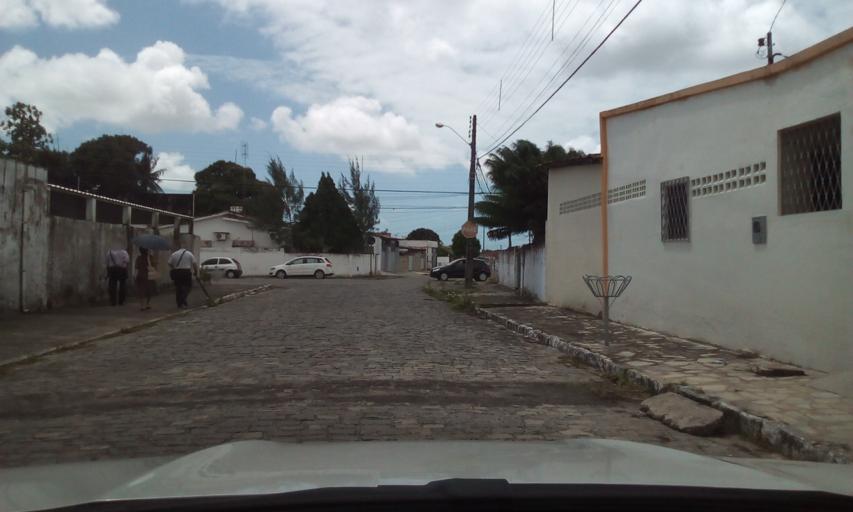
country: BR
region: Paraiba
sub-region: Joao Pessoa
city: Joao Pessoa
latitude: -7.1377
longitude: -34.8792
